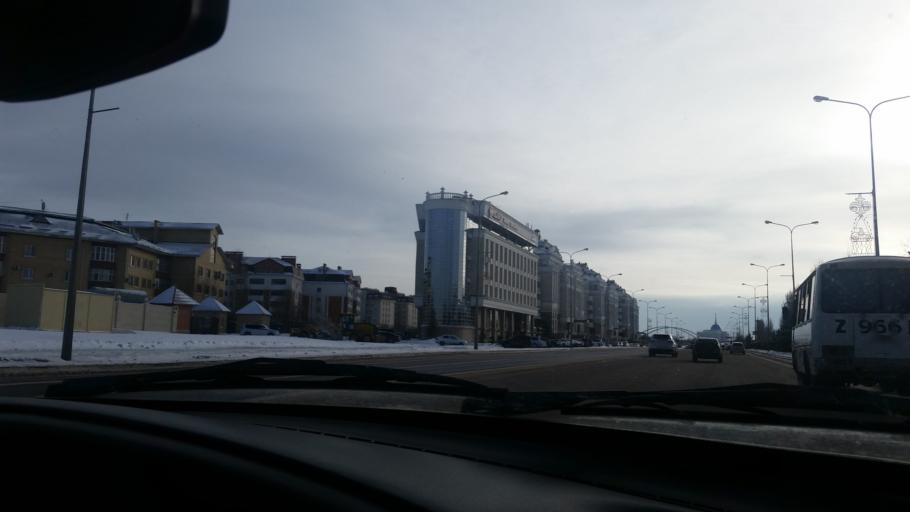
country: KZ
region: Astana Qalasy
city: Astana
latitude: 51.1461
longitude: 71.4448
